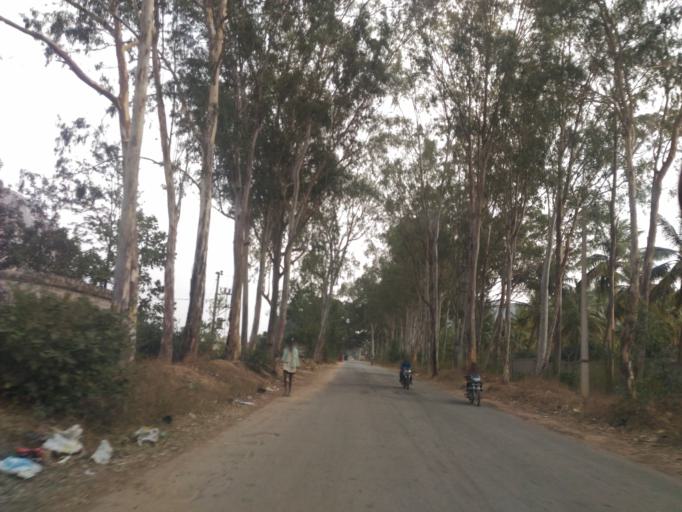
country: IN
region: Karnataka
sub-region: Chikkaballapur
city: Chik Ballapur
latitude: 13.3526
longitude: 77.6552
